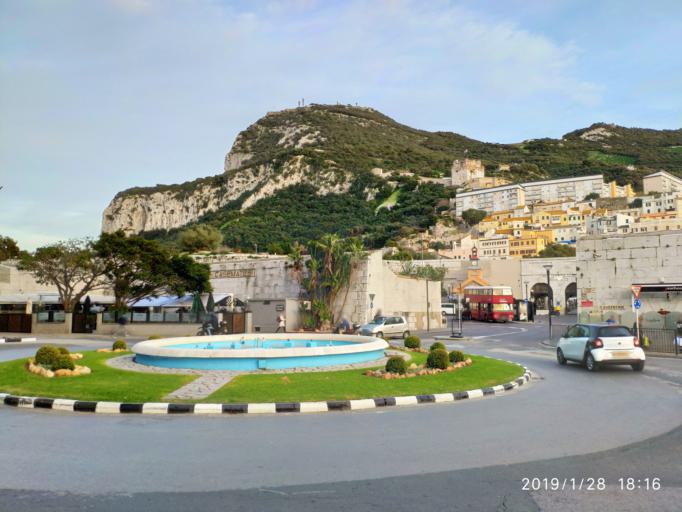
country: GI
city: Gibraltar
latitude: 36.1459
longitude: -5.3539
